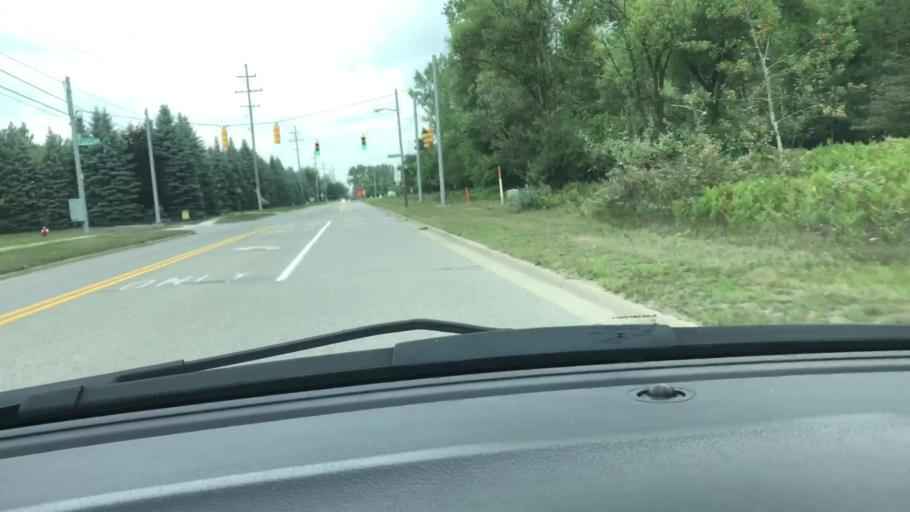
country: US
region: Michigan
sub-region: Midland County
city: Midland
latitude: 43.6204
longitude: -84.1874
